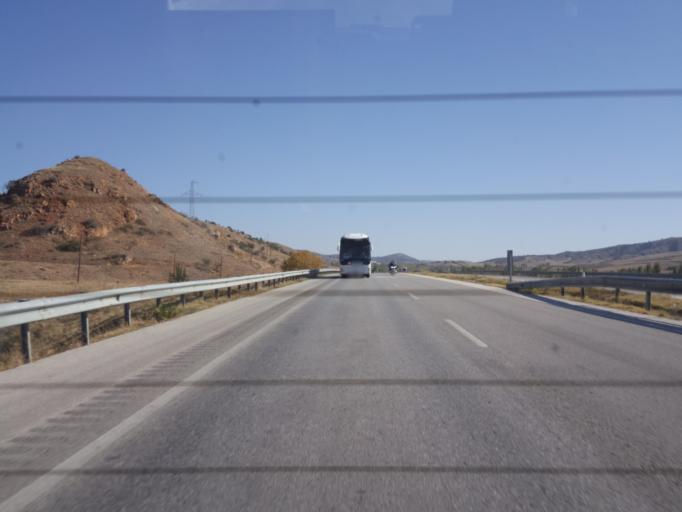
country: TR
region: Corum
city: Sungurlu
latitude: 40.2281
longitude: 34.5711
